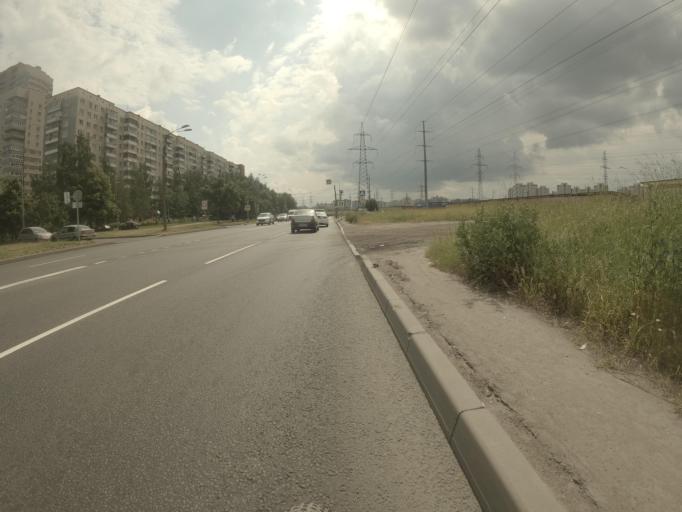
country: RU
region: St.-Petersburg
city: Krasnogvargeisky
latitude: 59.9396
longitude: 30.4675
